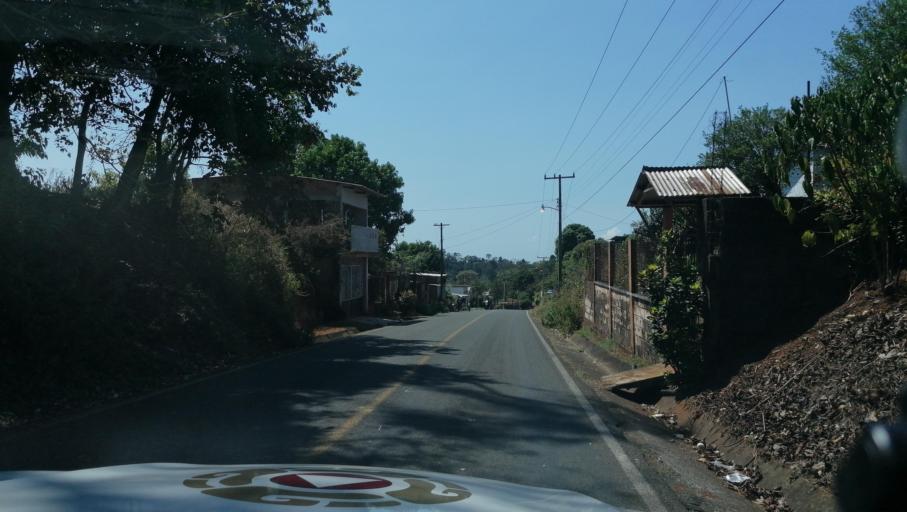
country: MX
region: Chiapas
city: Veinte de Noviembre
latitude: 14.9963
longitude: -92.2332
